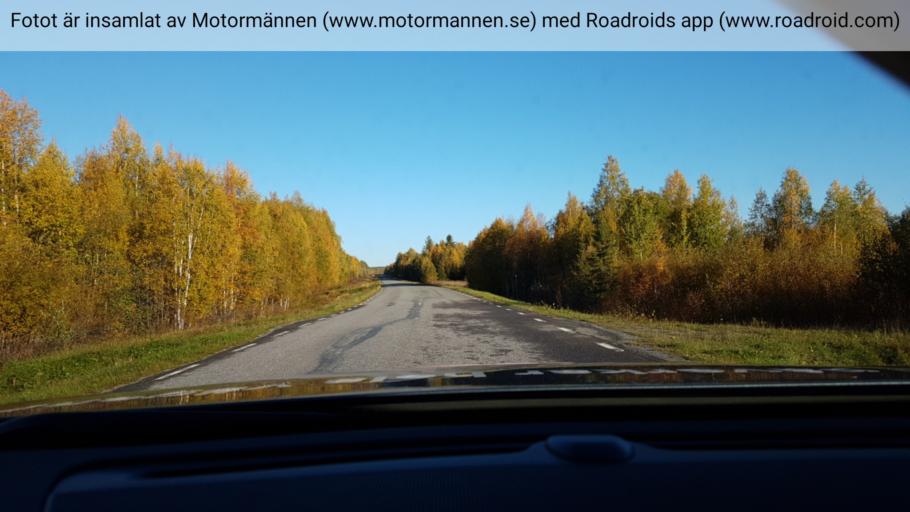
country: SE
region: Norrbotten
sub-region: Bodens Kommun
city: Boden
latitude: 65.9065
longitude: 21.6668
